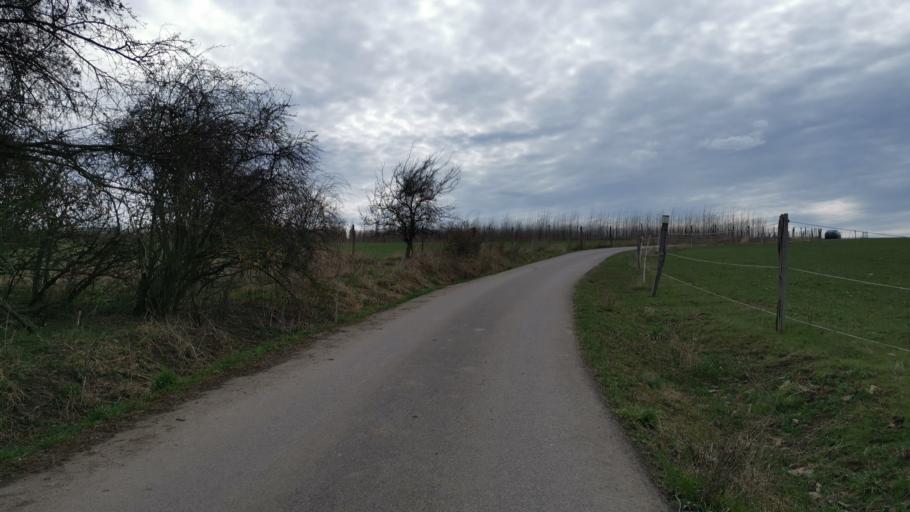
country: CZ
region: South Moravian
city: Petrov
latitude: 48.8453
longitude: 17.2981
